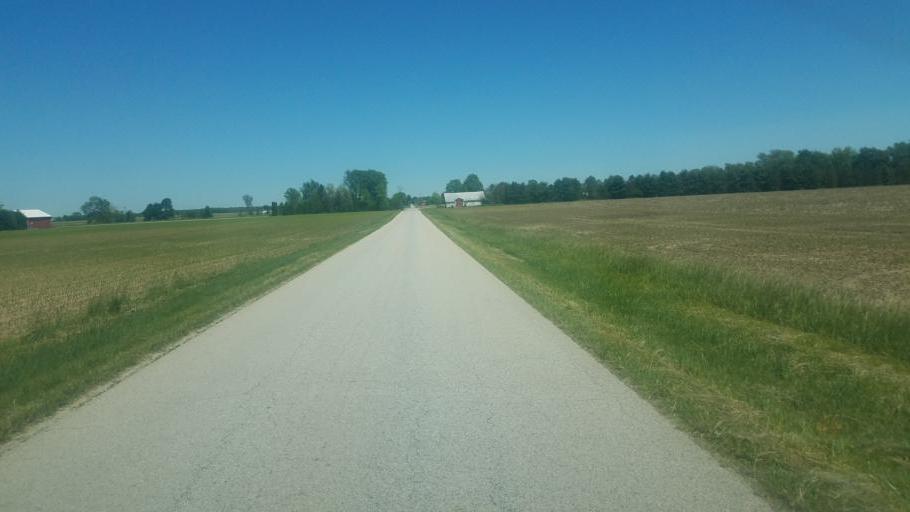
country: US
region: Ohio
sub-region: Shelby County
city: Sidney
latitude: 40.2003
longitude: -84.0646
